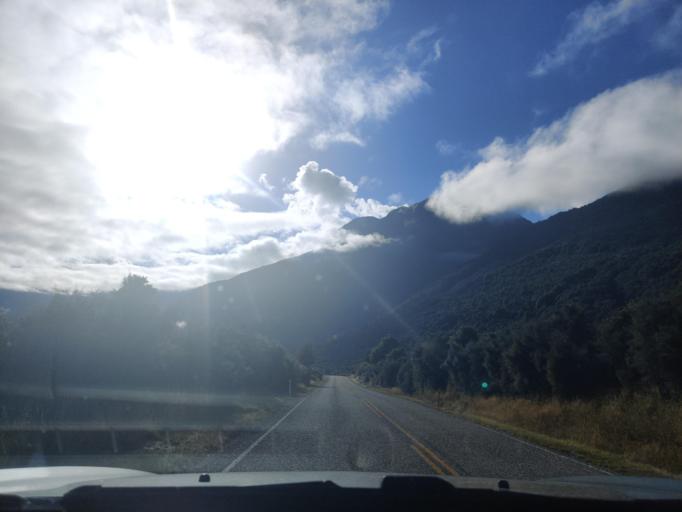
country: NZ
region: Otago
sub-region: Queenstown-Lakes District
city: Wanaka
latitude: -44.1610
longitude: 169.2838
